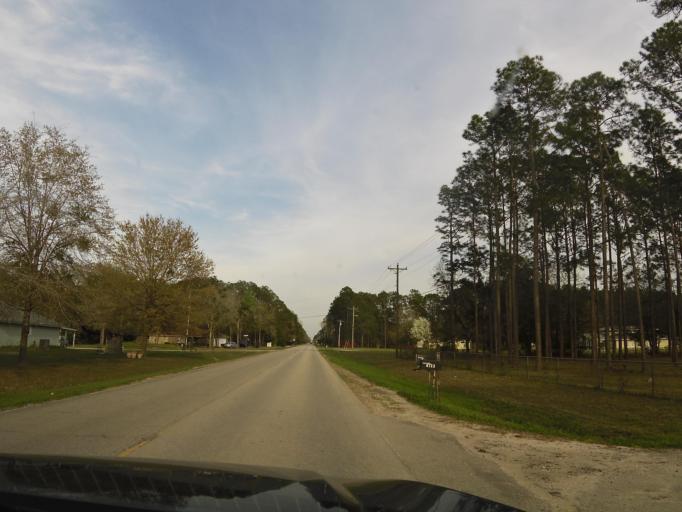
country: US
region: Florida
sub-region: Clay County
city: Middleburg
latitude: 30.1138
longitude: -81.8782
